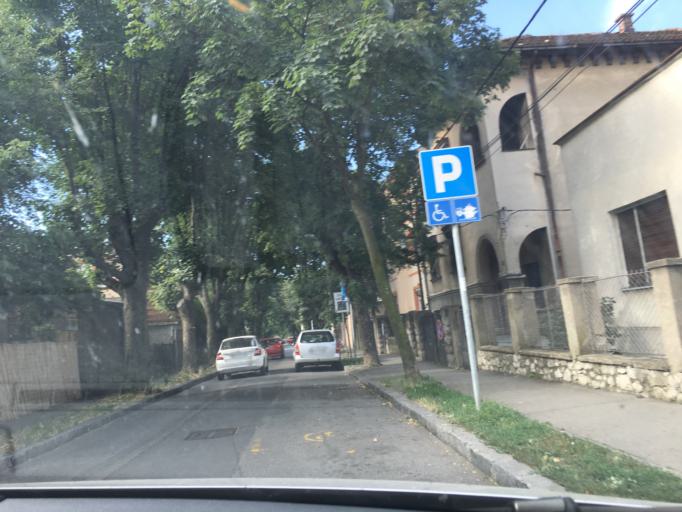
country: RS
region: Central Serbia
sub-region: Belgrade
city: Palilula
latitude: 44.7969
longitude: 20.5029
